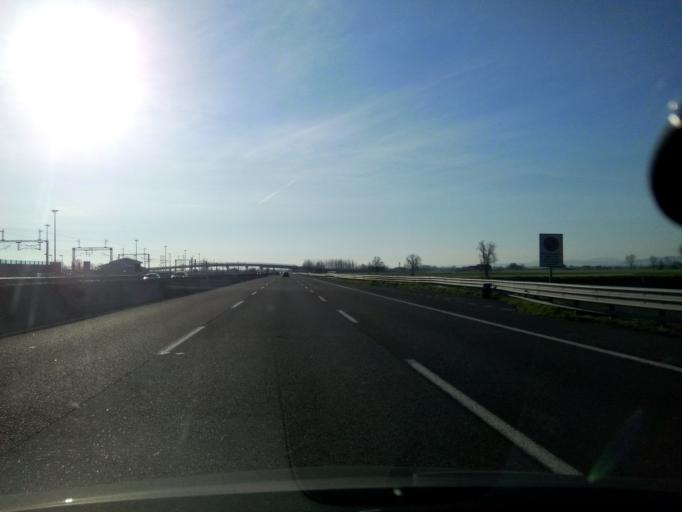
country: IT
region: Emilia-Romagna
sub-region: Provincia di Reggio Emilia
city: Campegine
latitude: 44.7605
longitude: 10.5354
